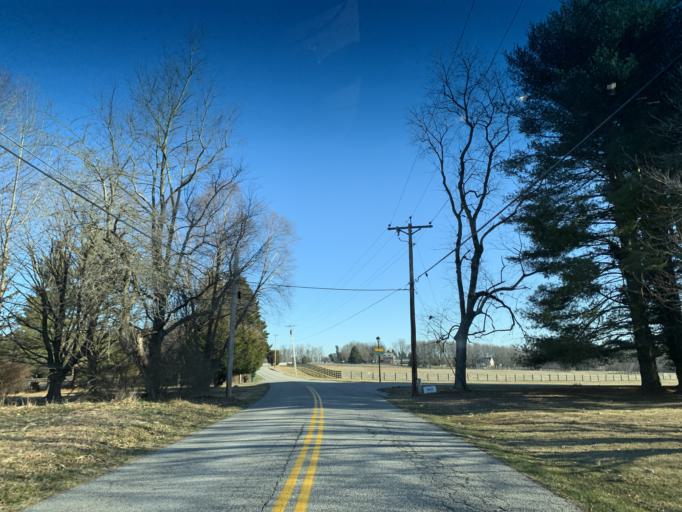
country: US
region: Maryland
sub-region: Harford County
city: Aberdeen
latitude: 39.5702
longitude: -76.2384
